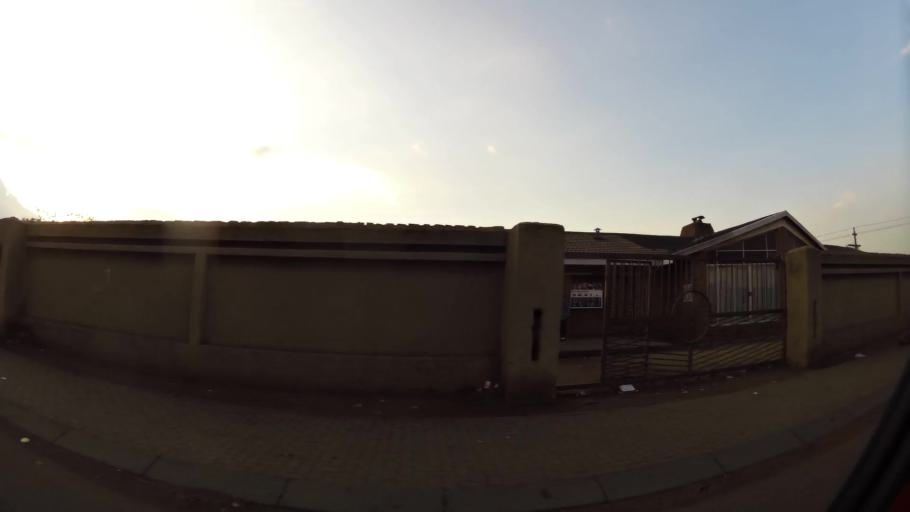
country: ZA
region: Gauteng
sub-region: City of Johannesburg Metropolitan Municipality
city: Orange Farm
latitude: -26.5361
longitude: 27.8386
